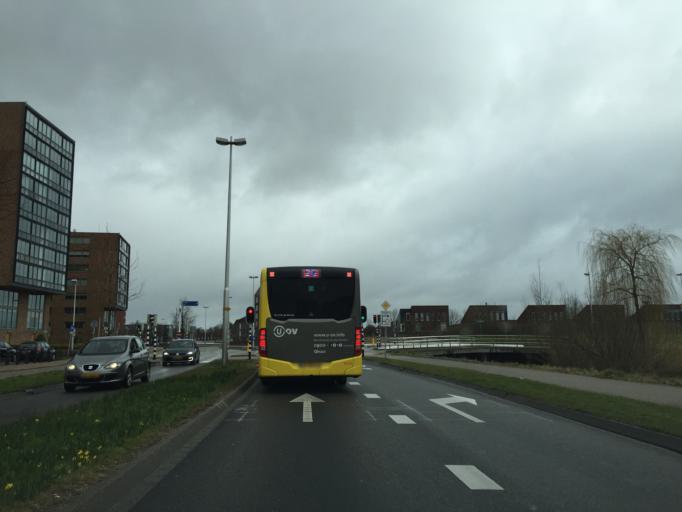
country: NL
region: Utrecht
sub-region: Stichtse Vecht
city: Maarssen
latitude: 52.0858
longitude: 5.0483
